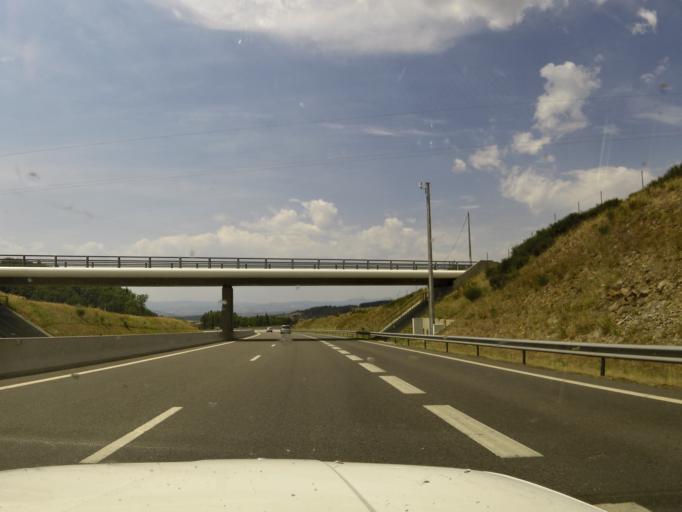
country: FR
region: Rhone-Alpes
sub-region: Departement de la Loire
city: Bussieres
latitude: 45.8712
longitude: 4.2910
